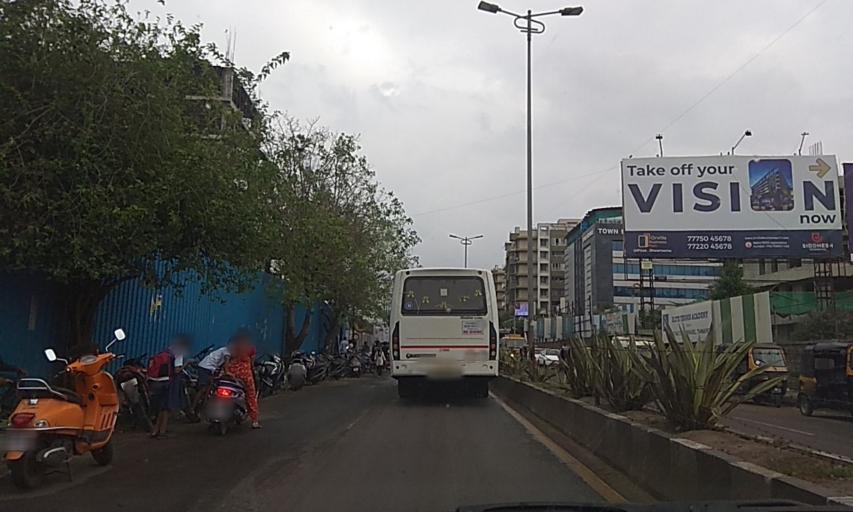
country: IN
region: Maharashtra
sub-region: Pune Division
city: Lohogaon
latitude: 18.5676
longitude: 73.9067
